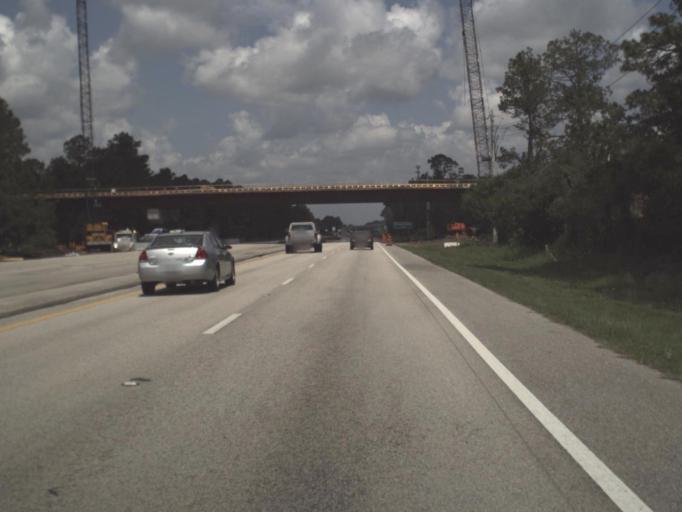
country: US
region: Florida
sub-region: Saint Johns County
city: Palm Valley
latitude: 30.0892
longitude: -81.4631
